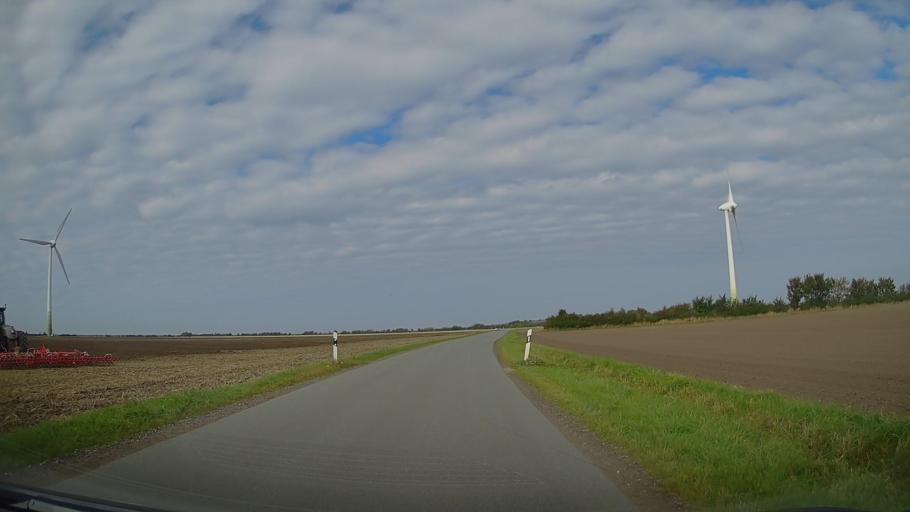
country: DE
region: Schleswig-Holstein
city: Grossenbrode
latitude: 54.5116
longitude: 11.0548
